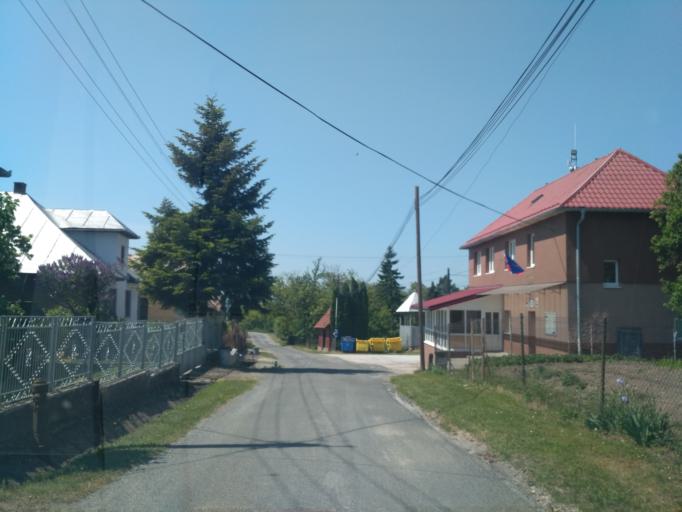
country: SK
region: Kosicky
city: Kosice
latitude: 48.8277
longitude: 21.4499
